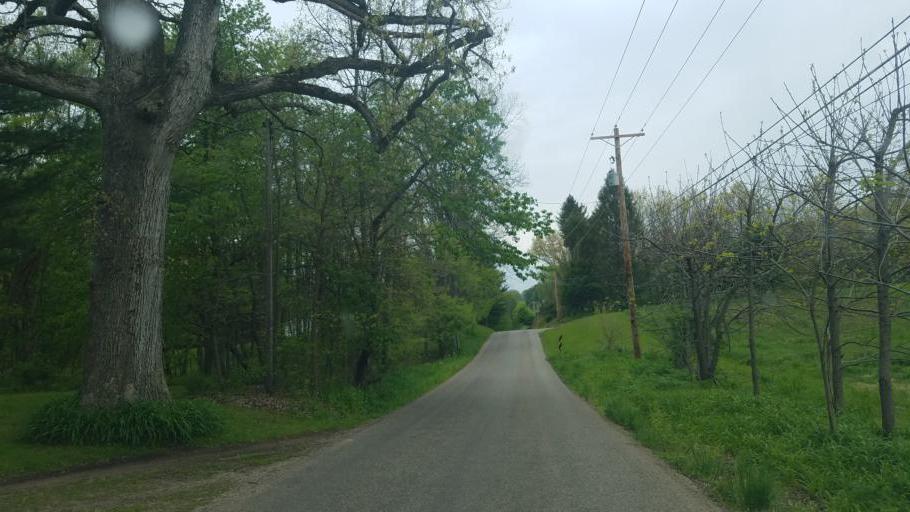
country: US
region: Ohio
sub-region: Knox County
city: Gambier
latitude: 40.3891
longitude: -82.3862
